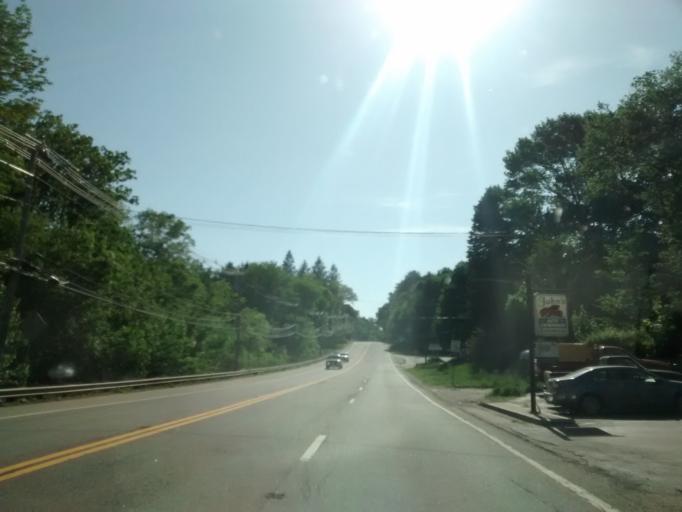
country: US
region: Massachusetts
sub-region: Worcester County
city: Charlton
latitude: 42.1446
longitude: -71.9959
